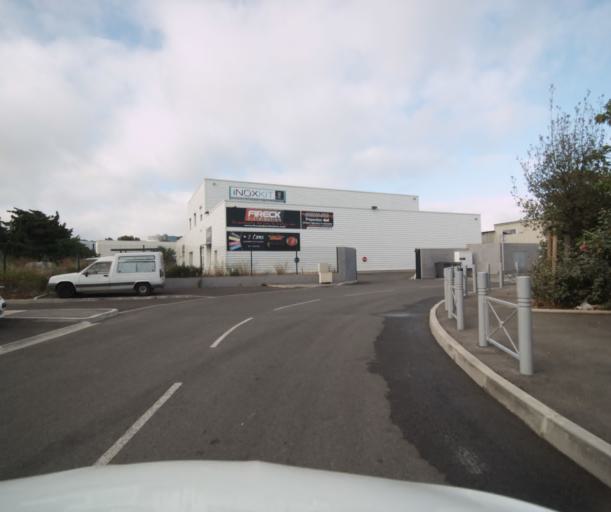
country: FR
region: Provence-Alpes-Cote d'Azur
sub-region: Departement du Var
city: Six-Fours-les-Plages
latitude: 43.1148
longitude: 5.8516
